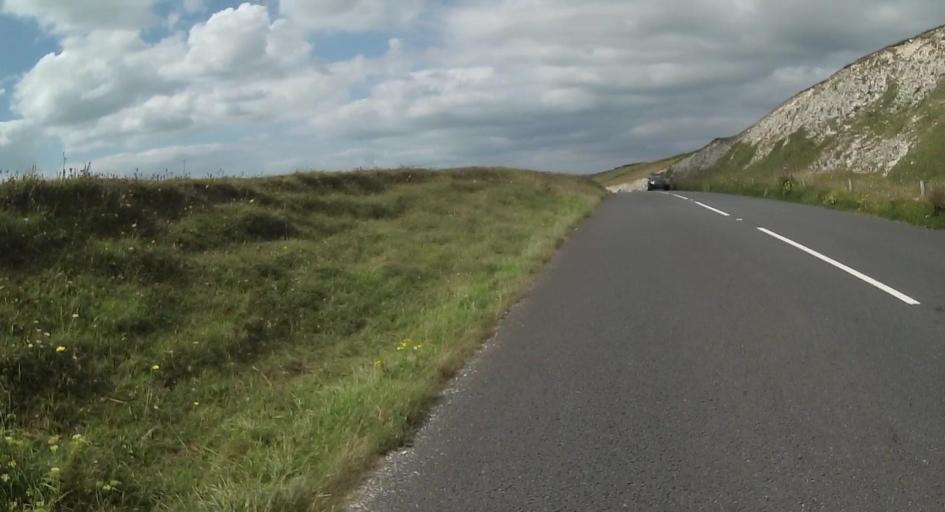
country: GB
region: England
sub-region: Isle of Wight
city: Freshwater
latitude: 50.6681
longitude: -1.4912
